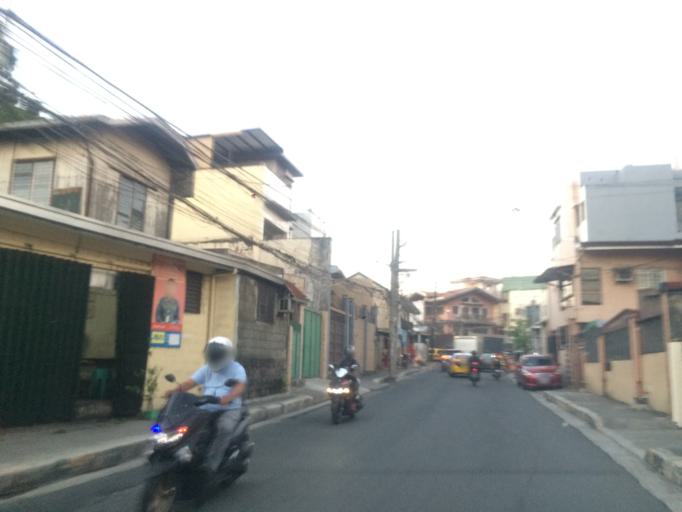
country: PH
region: Calabarzon
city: Del Monte
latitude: 14.6431
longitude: 121.0140
